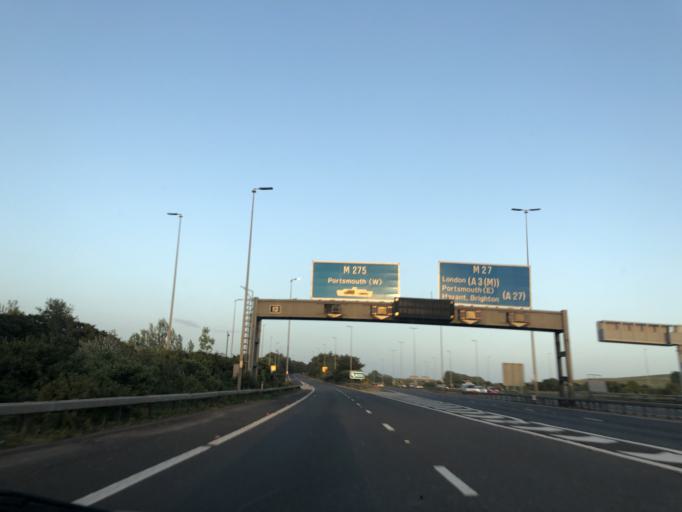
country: GB
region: England
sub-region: Portsmouth
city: Cosham
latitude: 50.8419
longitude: -1.0917
